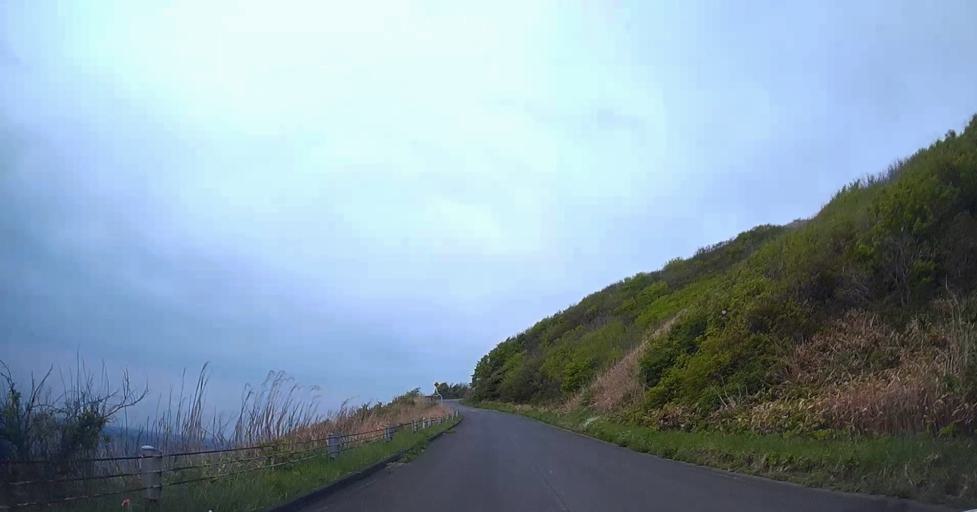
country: JP
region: Aomori
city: Shimokizukuri
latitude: 41.1946
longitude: 140.3366
